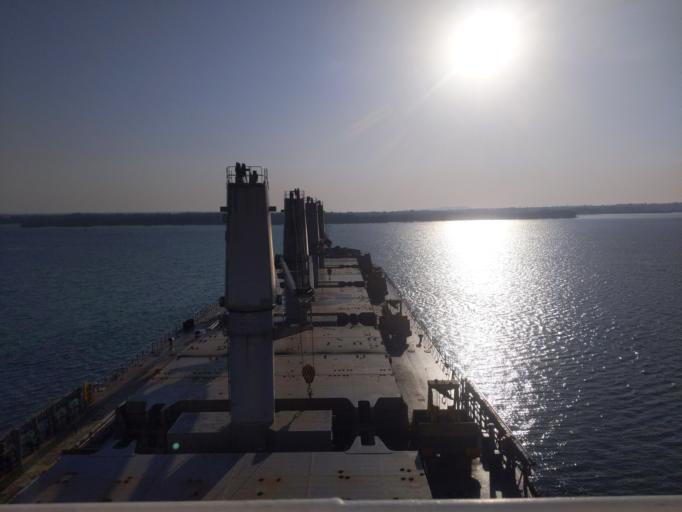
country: ZA
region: KwaZulu-Natal
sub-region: uThungulu District Municipality
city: Richards Bay
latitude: -28.8034
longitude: 32.0535
